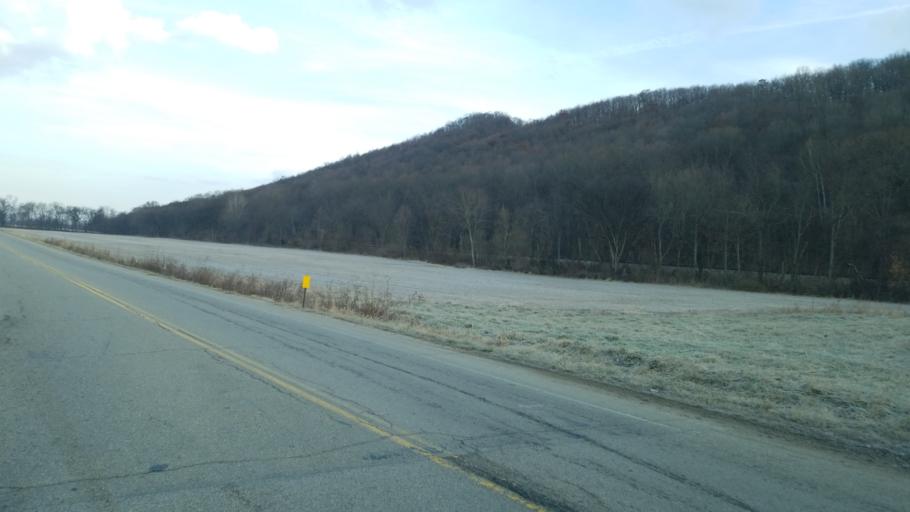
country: US
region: Ohio
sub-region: Pike County
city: Waverly
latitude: 39.2175
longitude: -82.8450
